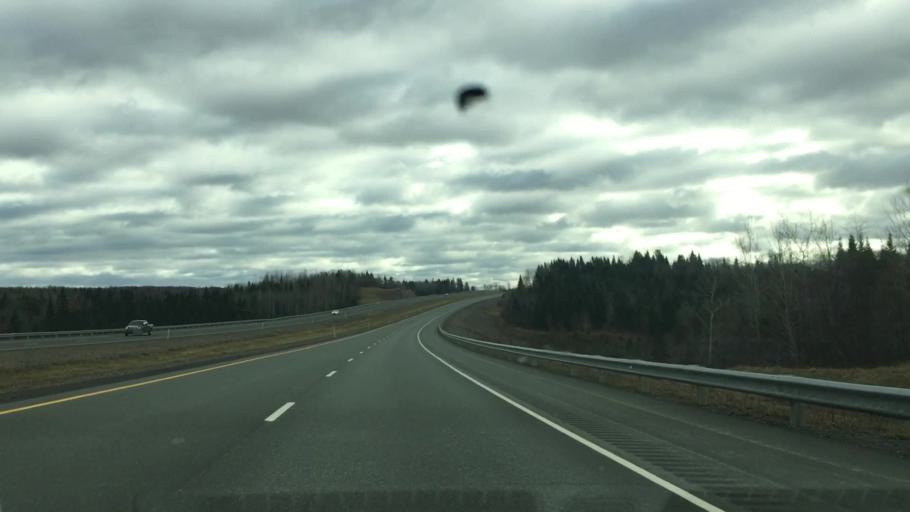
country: CA
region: New Brunswick
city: Florenceville-Bristol
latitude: 46.5415
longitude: -67.7145
